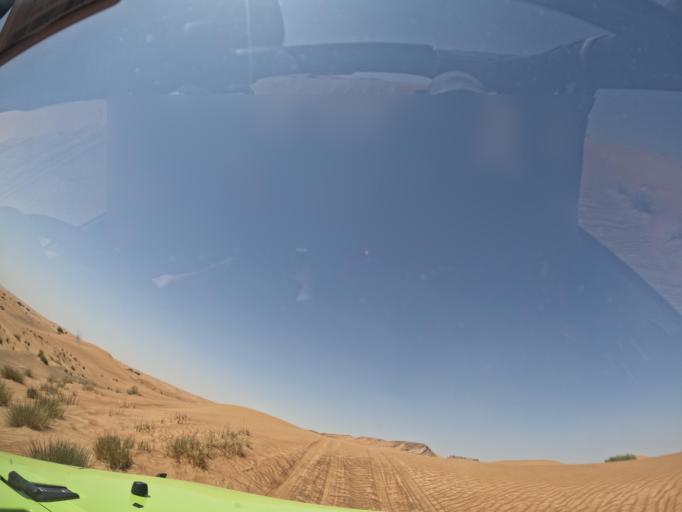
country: AE
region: Ash Shariqah
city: Adh Dhayd
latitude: 25.0190
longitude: 55.7432
